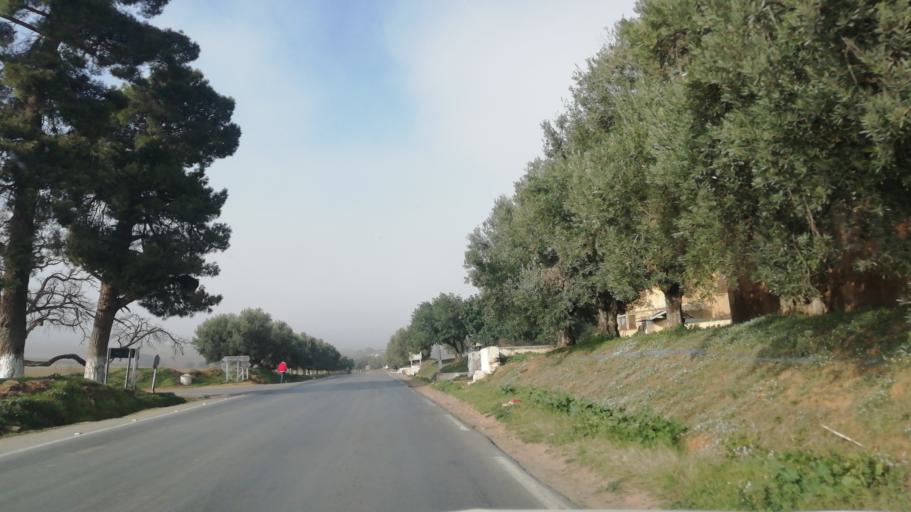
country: DZ
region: Mascara
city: Mascara
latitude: 35.5354
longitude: 0.3594
